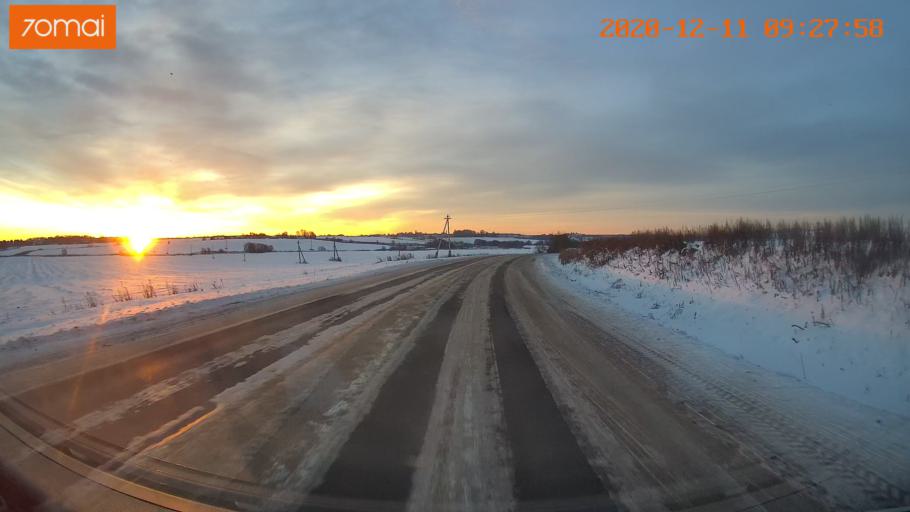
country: RU
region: Vologda
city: Vologda
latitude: 59.1583
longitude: 40.0106
